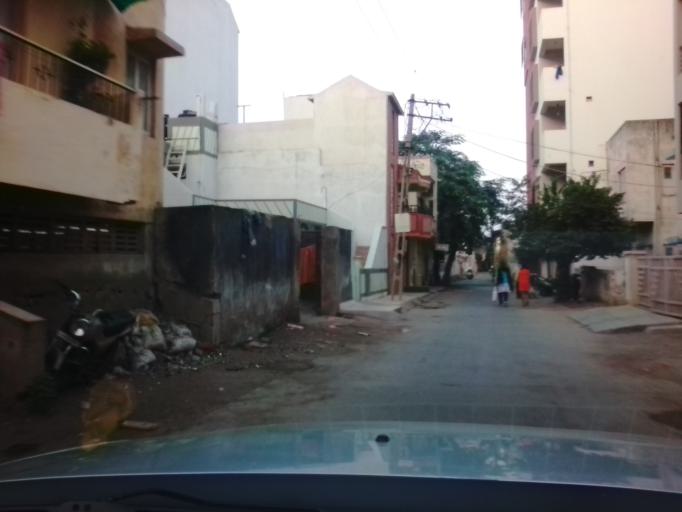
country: IN
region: Gujarat
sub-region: Jamnagar
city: Jamnagar
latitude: 22.4863
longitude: 70.0556
